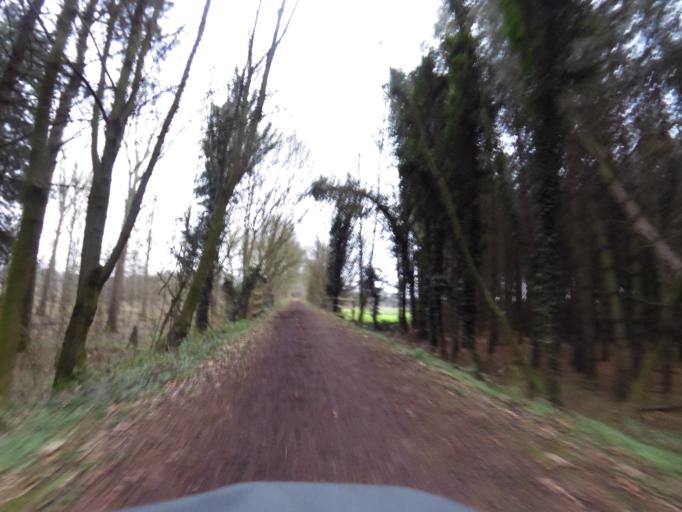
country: GB
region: England
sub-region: Norfolk
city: Costessey
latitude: 52.7162
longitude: 1.1376
